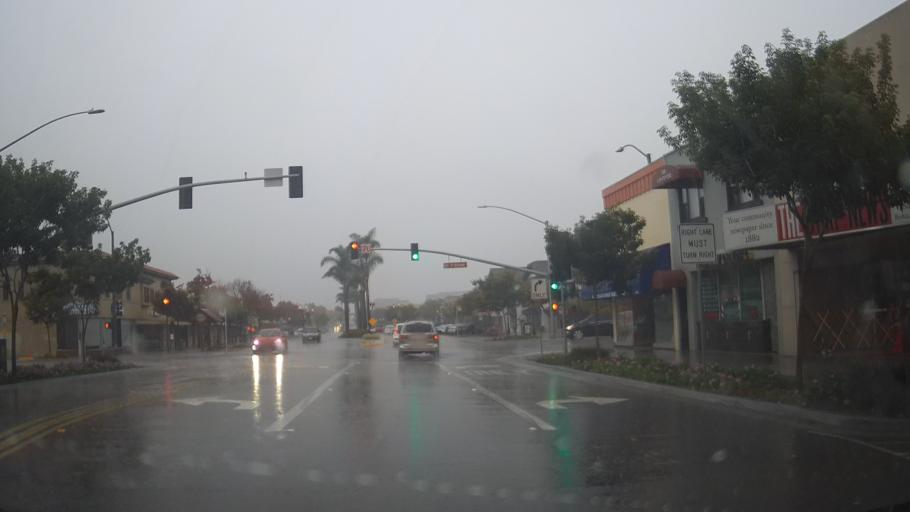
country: US
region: California
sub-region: San Diego County
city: Chula Vista
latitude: 32.6410
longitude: -117.0813
